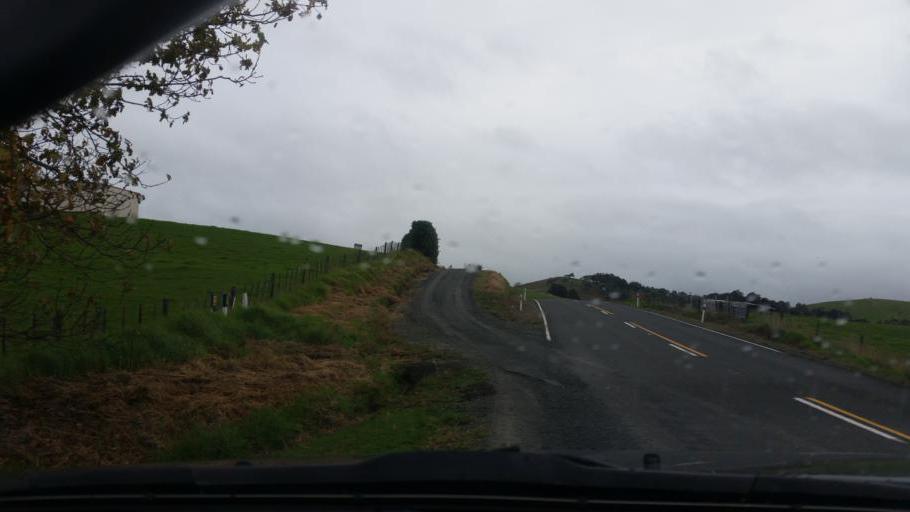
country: NZ
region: Northland
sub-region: Kaipara District
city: Dargaville
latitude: -36.0189
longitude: 173.9840
